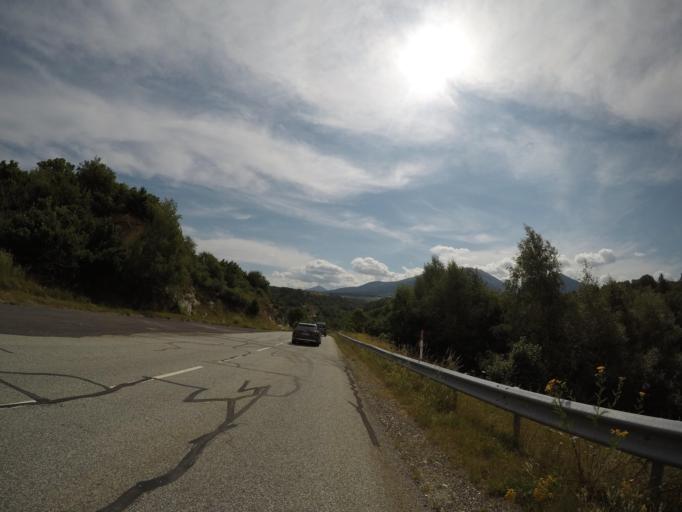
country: ES
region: Catalonia
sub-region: Provincia de Girona
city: Llivia
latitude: 42.4856
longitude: 2.0539
